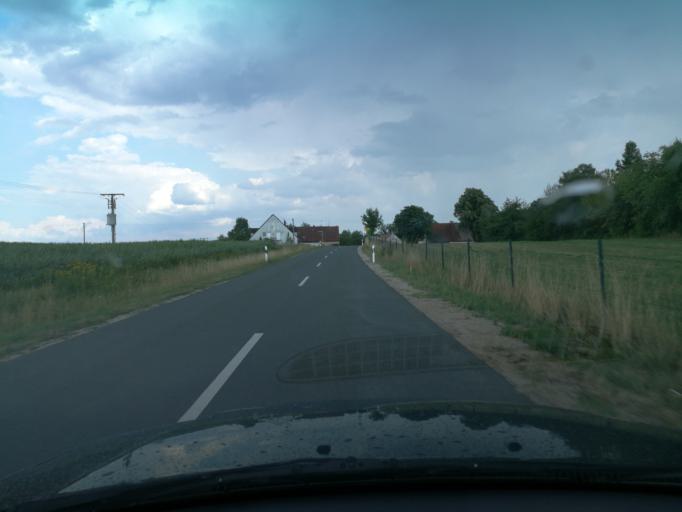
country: DE
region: Bavaria
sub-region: Regierungsbezirk Mittelfranken
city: Langenzenn
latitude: 49.4664
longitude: 10.7878
